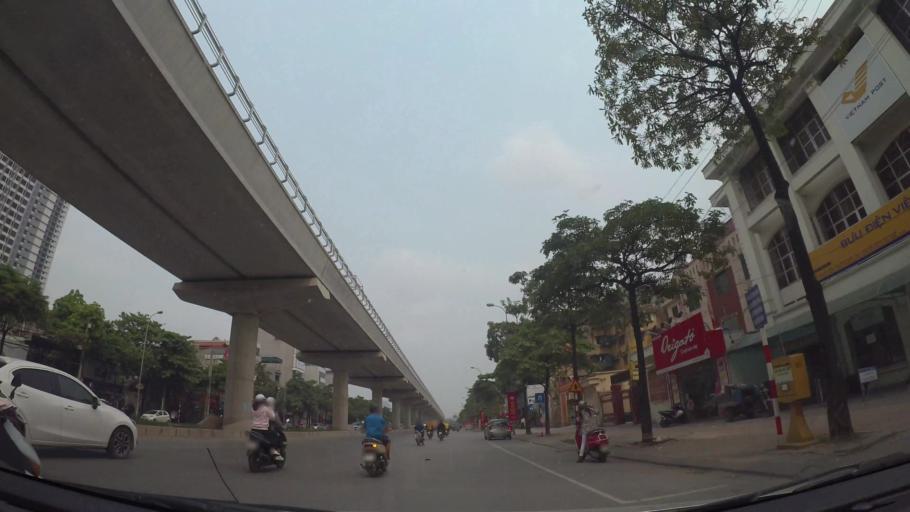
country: VN
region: Ha Noi
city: Cau Dien
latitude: 21.0402
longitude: 105.7651
